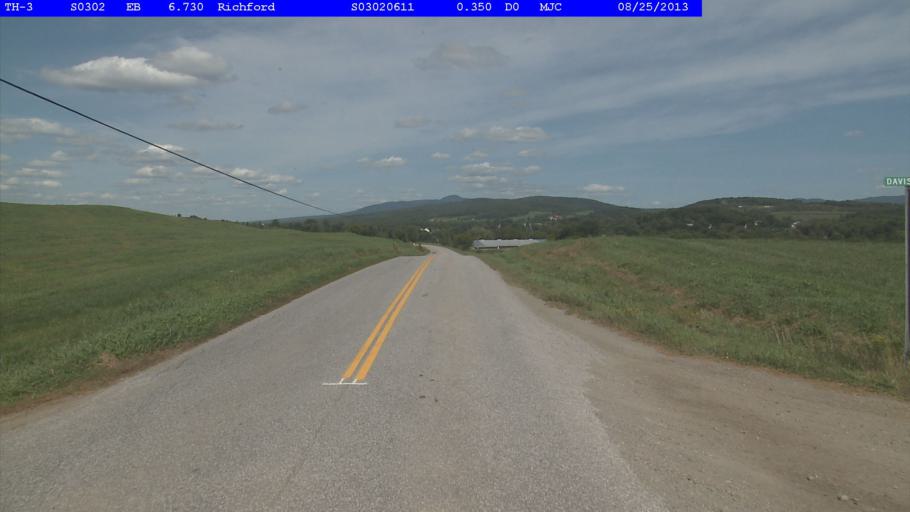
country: US
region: Vermont
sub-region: Franklin County
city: Richford
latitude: 44.9917
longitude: -72.6887
